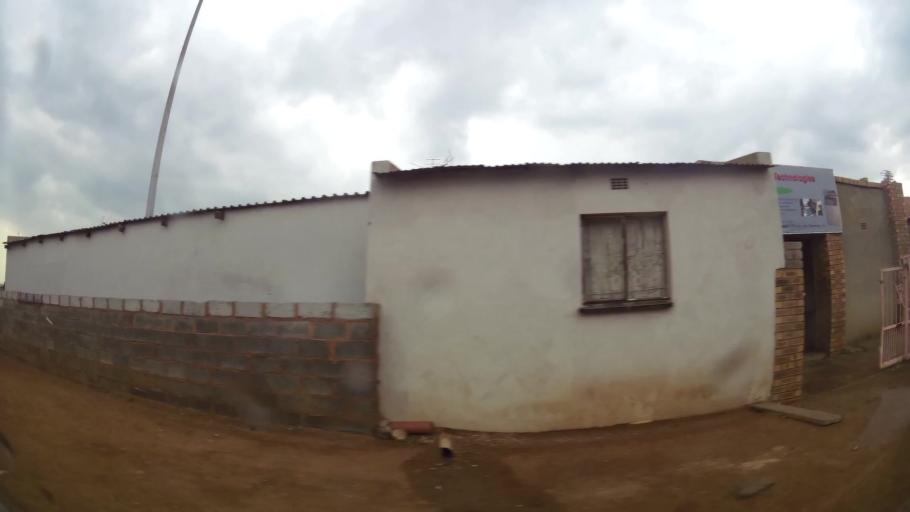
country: ZA
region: Gauteng
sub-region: Ekurhuleni Metropolitan Municipality
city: Germiston
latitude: -26.3613
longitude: 28.1566
